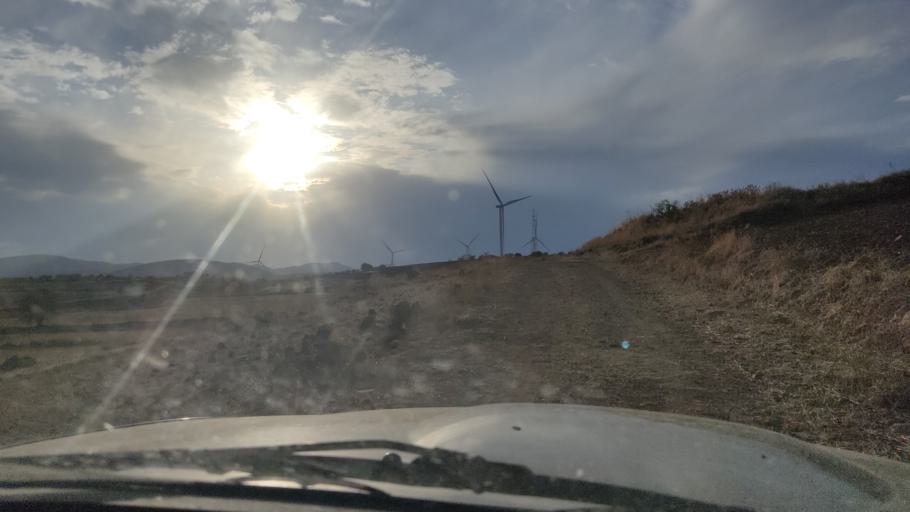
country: ES
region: Aragon
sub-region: Provincia de Teruel
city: Monforte de Moyuela
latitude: 41.0716
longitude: -0.9986
